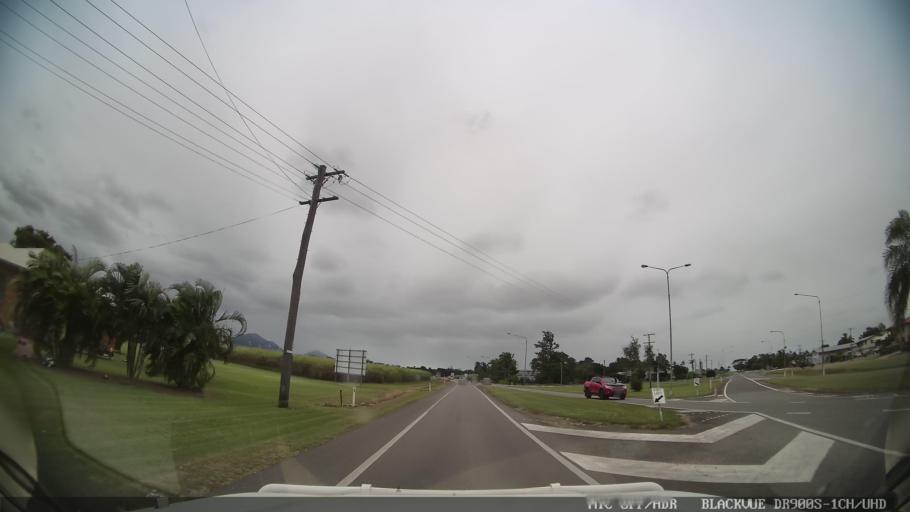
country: AU
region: Queensland
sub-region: Hinchinbrook
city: Ingham
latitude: -18.6412
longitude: 146.1636
